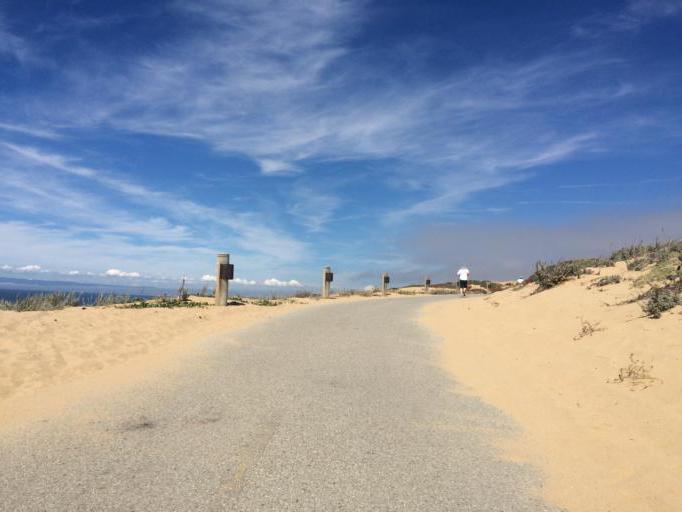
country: US
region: California
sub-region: Monterey County
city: Seaside
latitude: 36.6234
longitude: -121.8454
